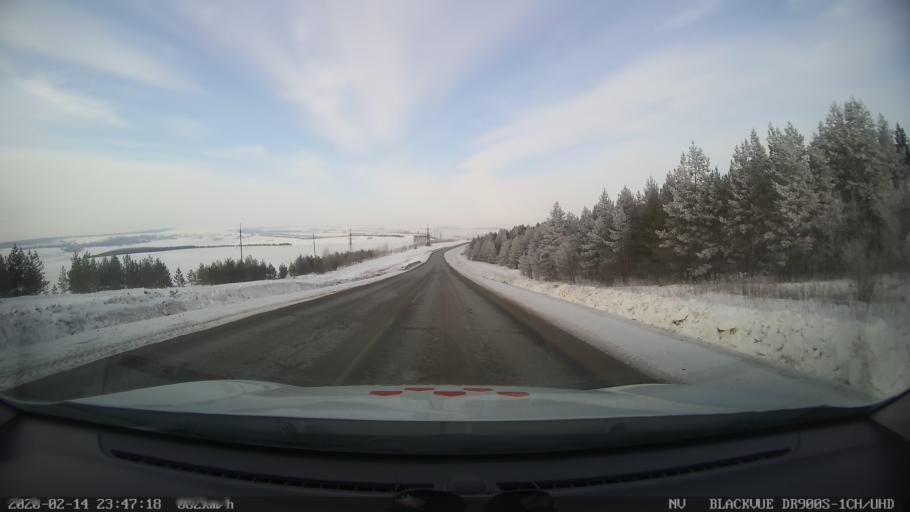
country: RU
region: Tatarstan
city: Kuybyshevskiy Zaton
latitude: 55.2370
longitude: 49.2102
